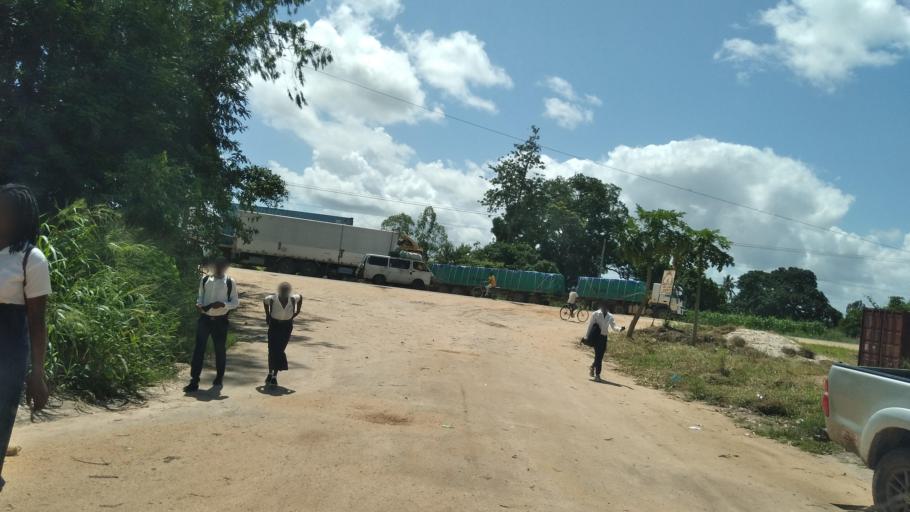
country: MZ
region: Zambezia
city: Quelimane
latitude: -17.5986
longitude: 36.8092
